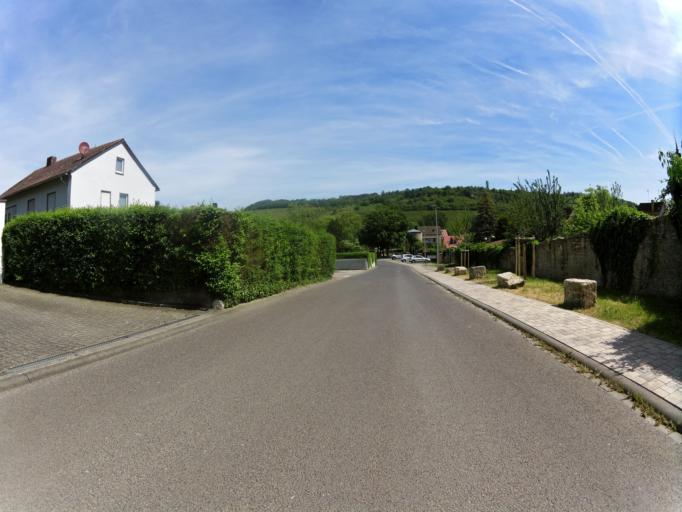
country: DE
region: Bavaria
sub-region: Regierungsbezirk Unterfranken
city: Sommerhausen
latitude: 49.6814
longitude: 10.0272
